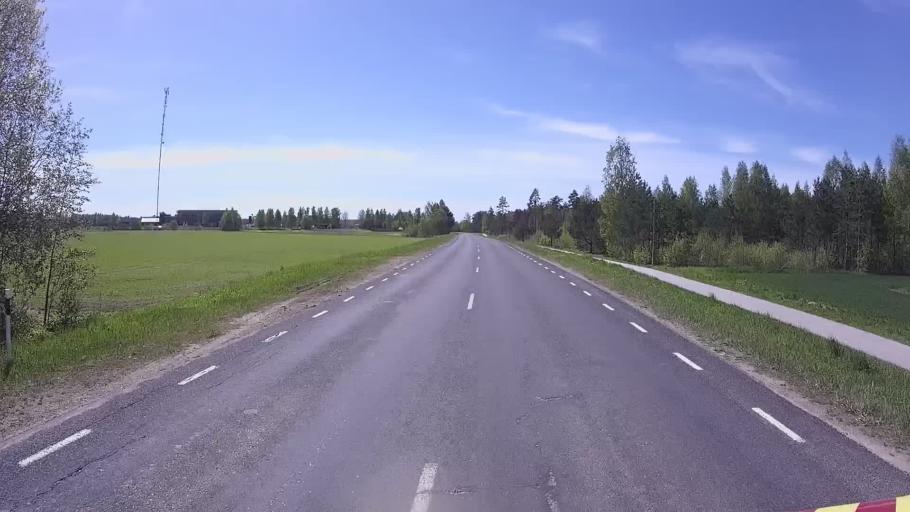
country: EE
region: Polvamaa
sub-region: Raepina vald
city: Rapina
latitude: 57.9990
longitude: 27.3393
